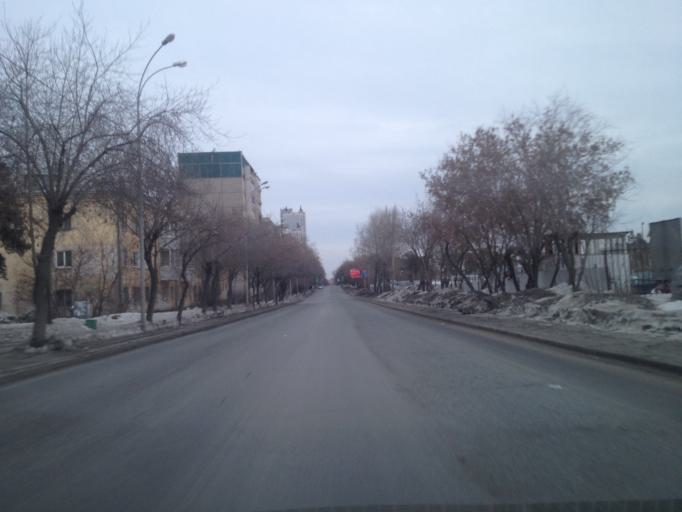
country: RU
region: Sverdlovsk
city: Sovkhoznyy
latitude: 56.7589
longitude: 60.6109
